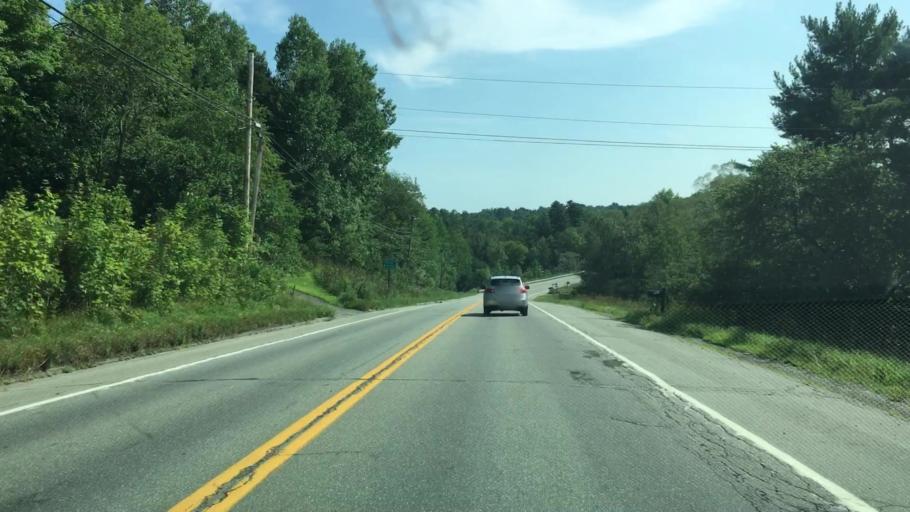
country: US
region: Maine
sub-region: Penobscot County
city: Orrington
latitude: 44.7017
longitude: -68.8443
